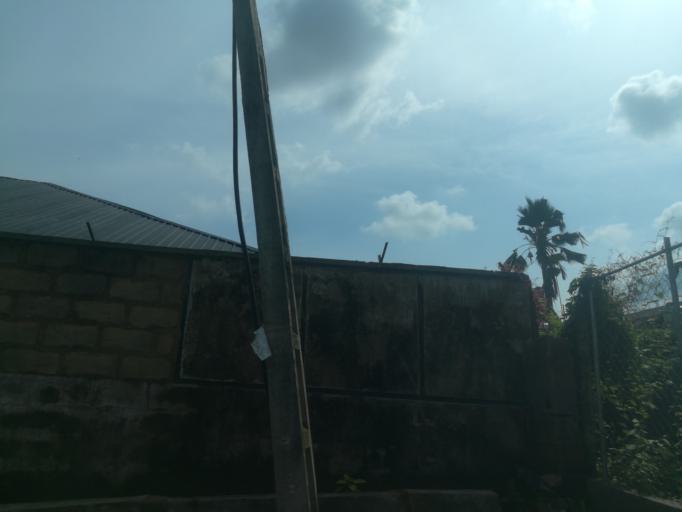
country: NG
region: Oyo
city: Ibadan
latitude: 7.3721
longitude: 3.8358
